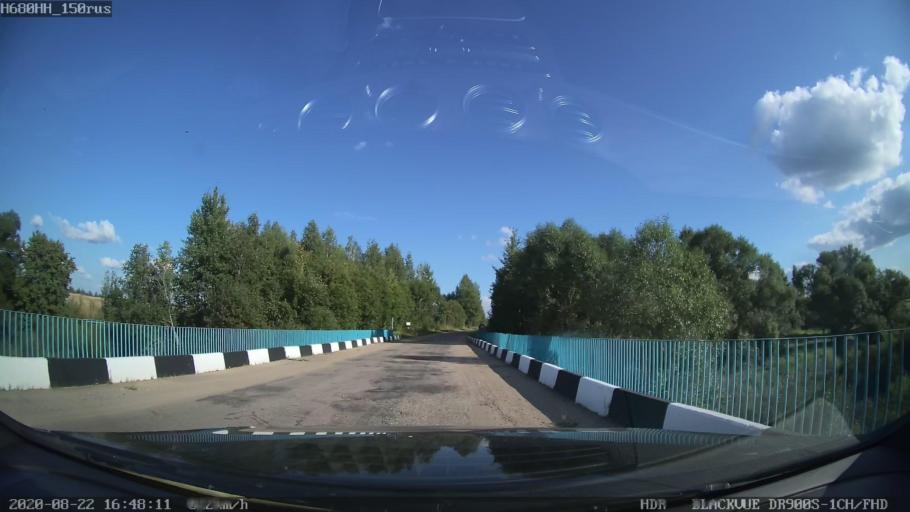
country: RU
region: Tverskaya
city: Rameshki
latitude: 57.2861
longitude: 36.0898
